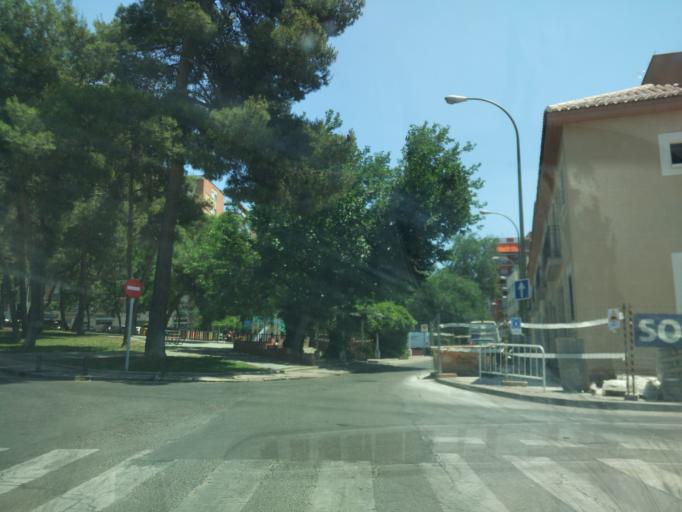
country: ES
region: Madrid
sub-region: Provincia de Madrid
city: Chamartin
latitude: 40.4733
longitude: -3.6905
